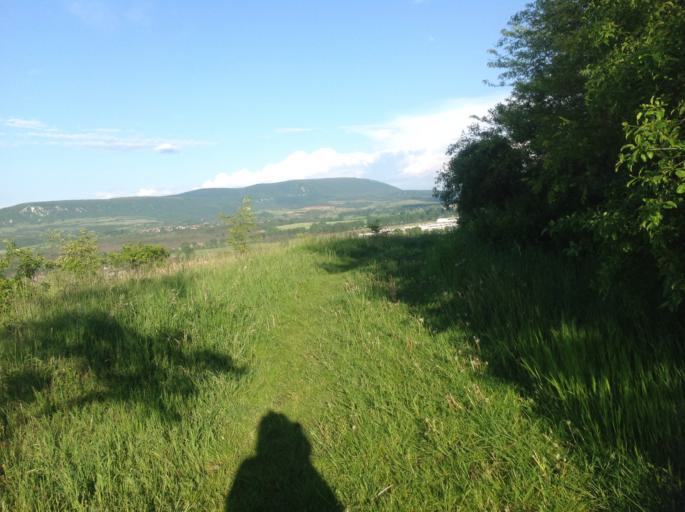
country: HU
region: Komarom-Esztergom
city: Dorog
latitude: 47.7154
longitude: 18.7276
